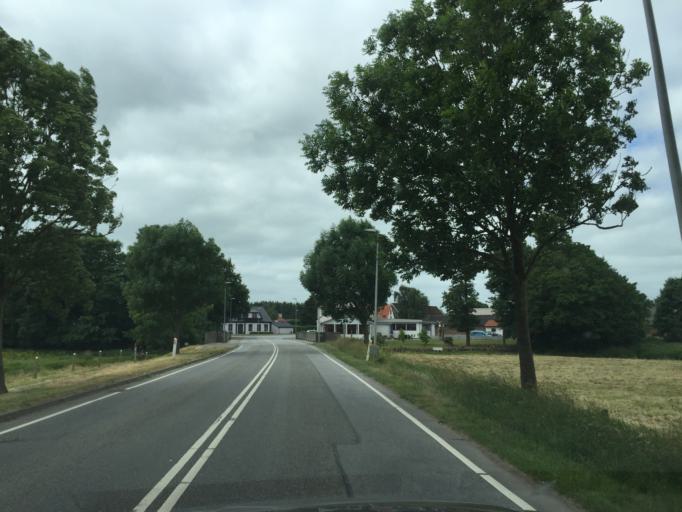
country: DK
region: South Denmark
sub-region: Vejen Kommune
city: Brorup
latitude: 55.4403
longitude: 8.9979
